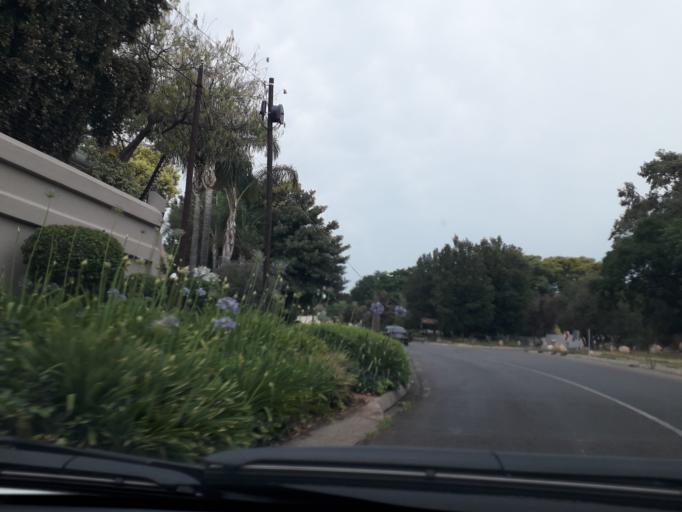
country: ZA
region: Gauteng
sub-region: City of Johannesburg Metropolitan Municipality
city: Johannesburg
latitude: -26.0891
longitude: 28.0375
